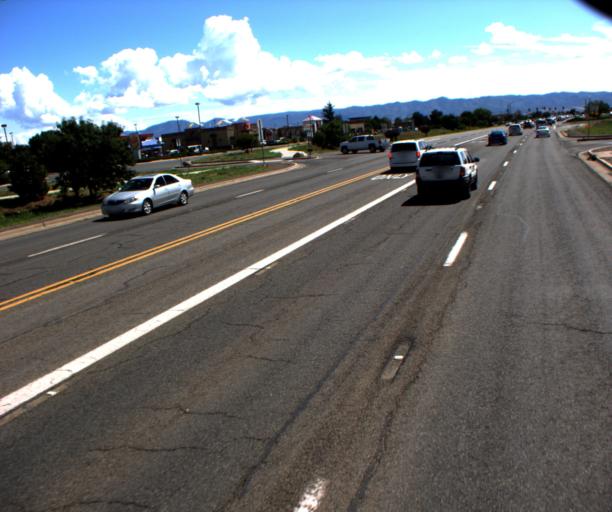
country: US
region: Arizona
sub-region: Yavapai County
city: Prescott Valley
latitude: 34.5854
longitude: -112.3303
